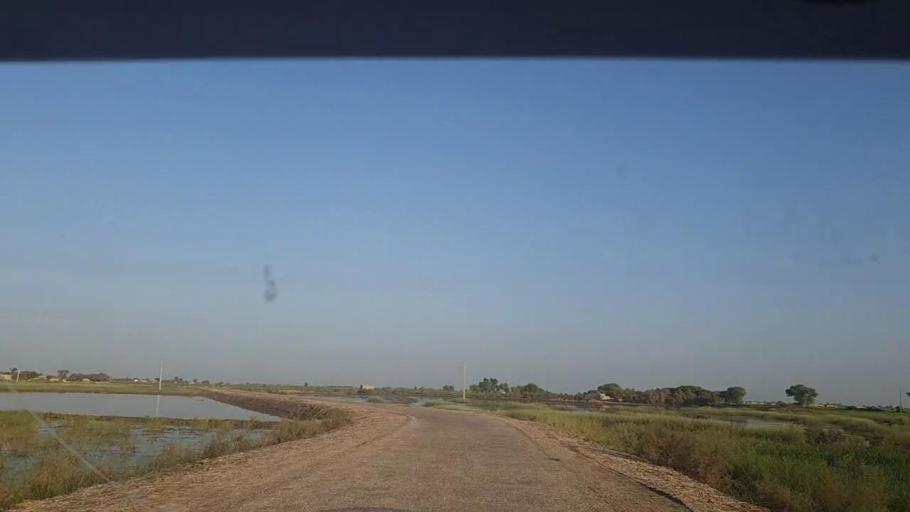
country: PK
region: Sindh
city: Thul
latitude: 28.1844
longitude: 68.8769
